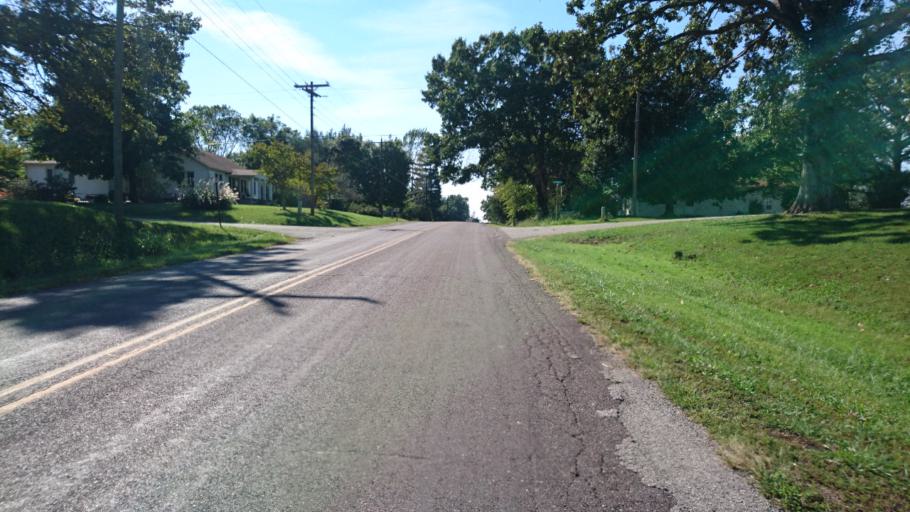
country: US
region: Missouri
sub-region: Crawford County
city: Bourbon
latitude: 38.1577
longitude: -91.2388
